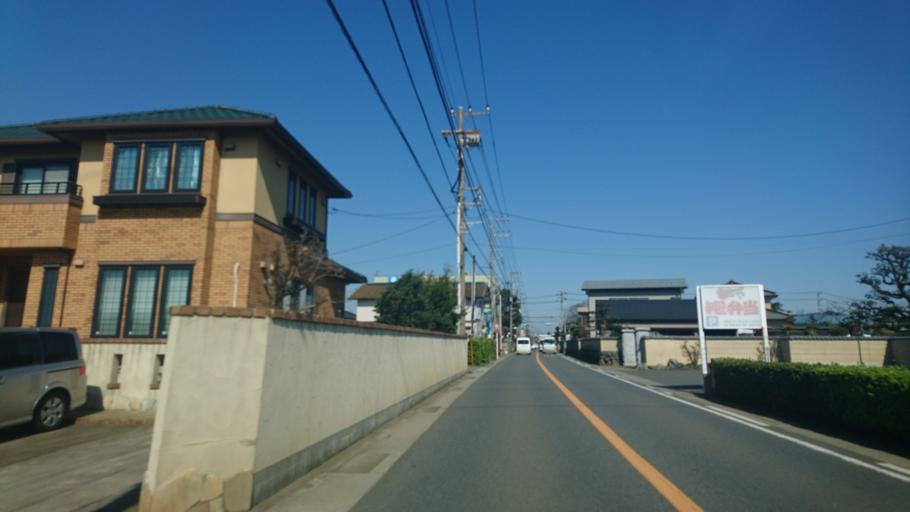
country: JP
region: Kanagawa
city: Fujisawa
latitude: 35.3805
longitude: 139.4818
